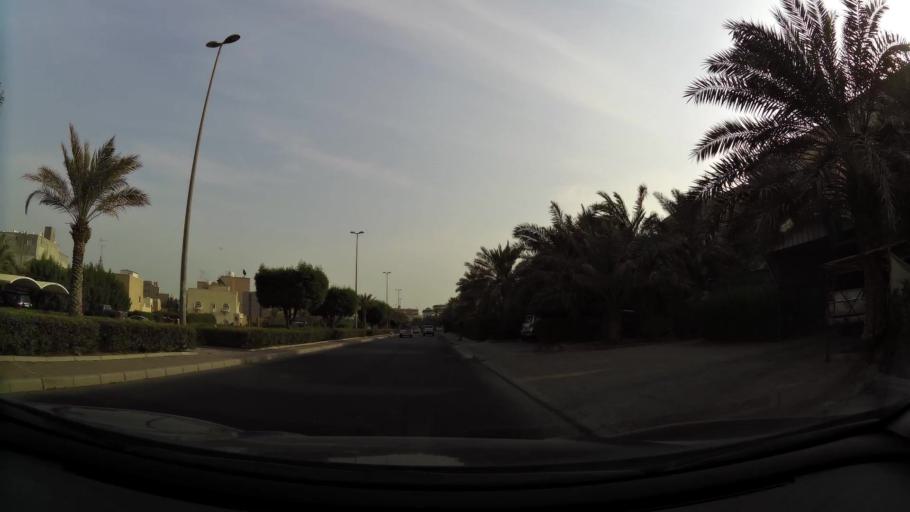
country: KW
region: Mubarak al Kabir
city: Sabah as Salim
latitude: 29.2191
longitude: 48.0619
